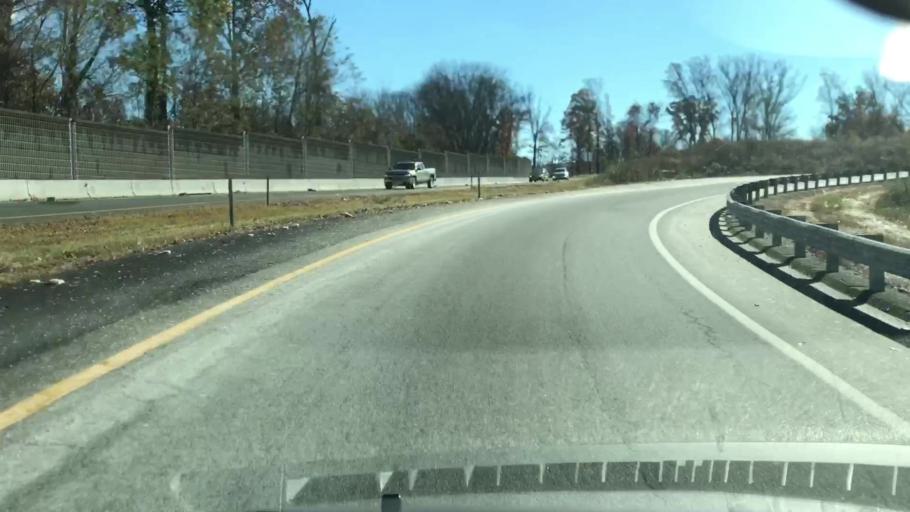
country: US
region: Virginia
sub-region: Fairfax County
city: Ravensworth
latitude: 38.8125
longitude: -77.2161
